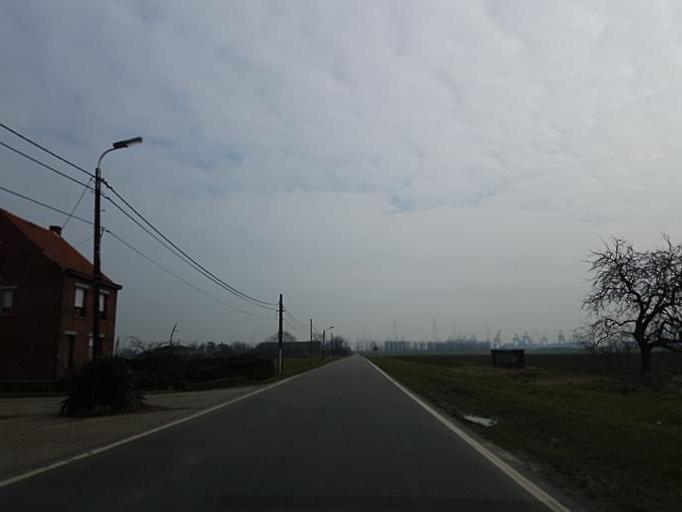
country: BE
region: Flanders
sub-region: Provincie Oost-Vlaanderen
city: Beveren
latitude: 51.3025
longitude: 4.2229
